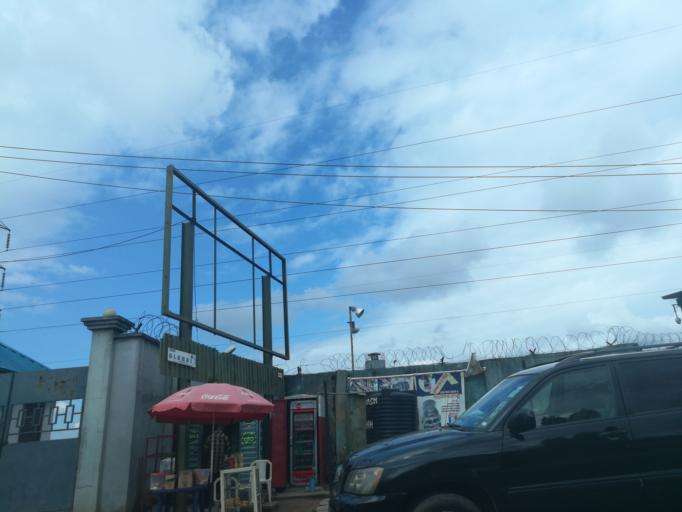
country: NG
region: Lagos
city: Agege
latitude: 6.6248
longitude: 3.3349
